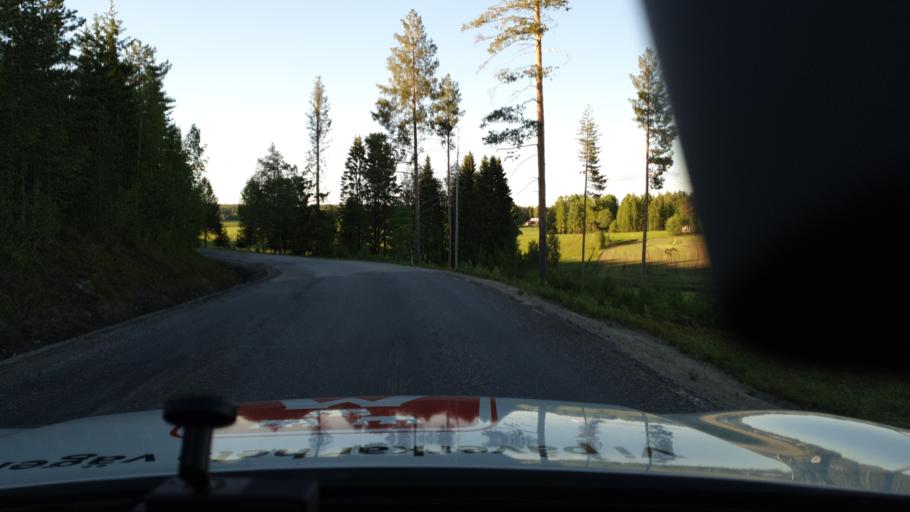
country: SE
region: Vaesterbotten
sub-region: Umea Kommun
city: Roback
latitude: 64.0205
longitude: 20.0851
